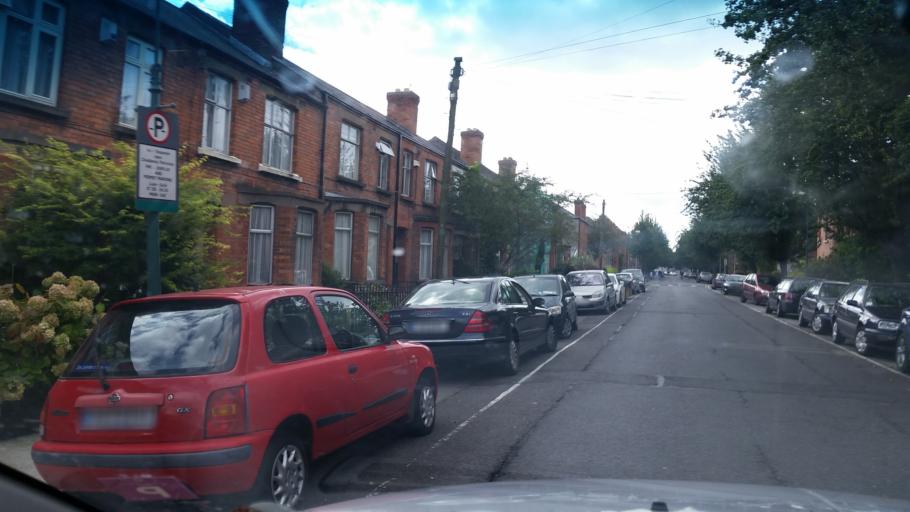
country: IE
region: Leinster
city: Rialto
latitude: 53.3335
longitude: -6.2793
